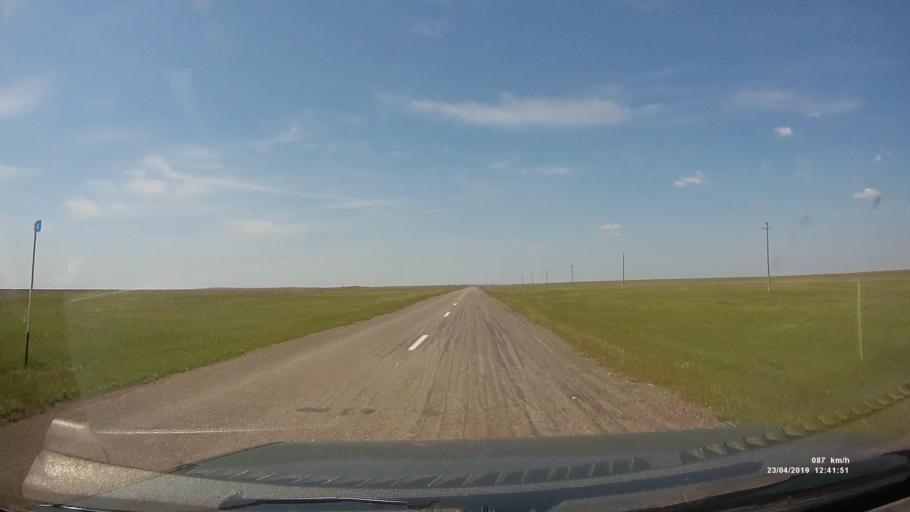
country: RU
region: Kalmykiya
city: Yashalta
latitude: 46.4513
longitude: 42.6747
